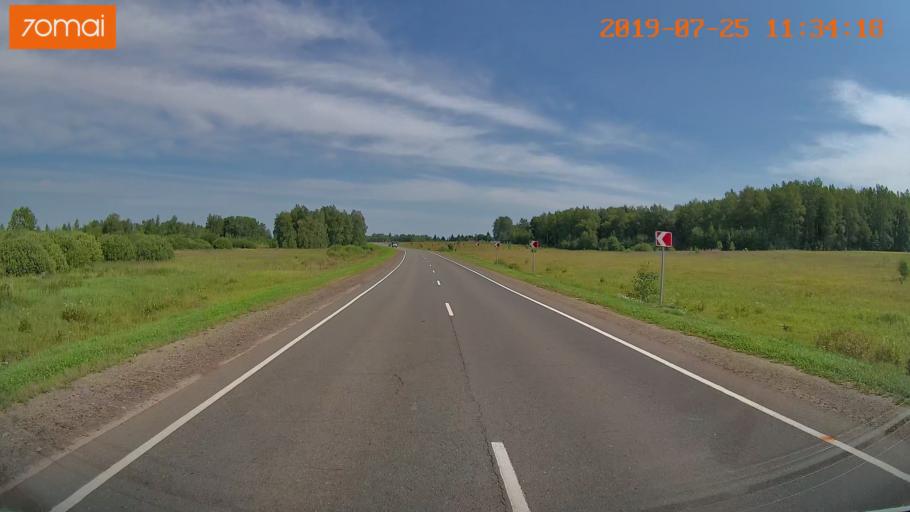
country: RU
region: Ivanovo
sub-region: Privolzhskiy Rayon
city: Ples
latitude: 57.3983
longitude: 41.4098
